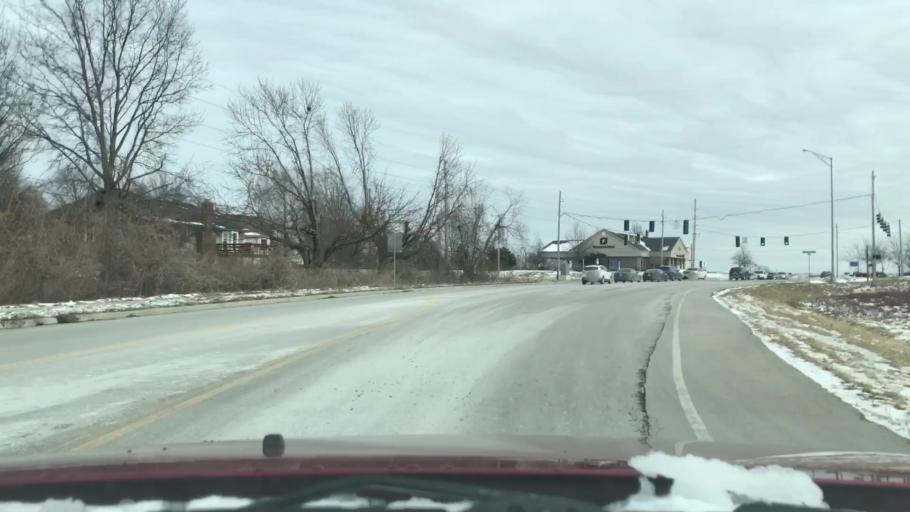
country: US
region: Missouri
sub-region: Jackson County
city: Lees Summit
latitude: 38.9038
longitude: -94.3410
